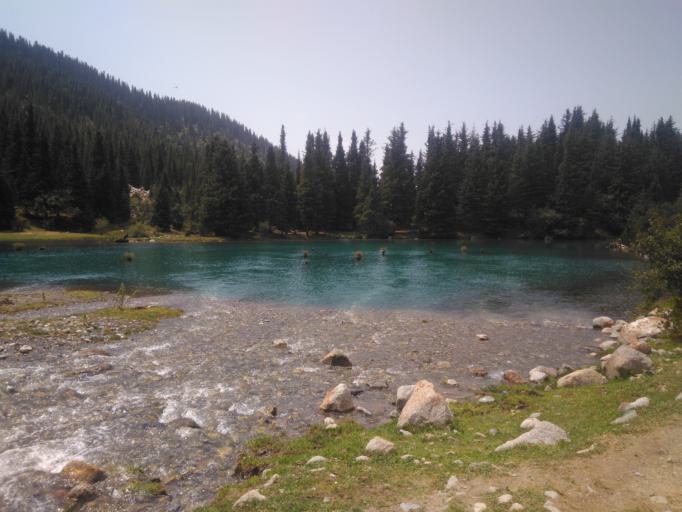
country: KG
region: Ysyk-Koel
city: Cholpon-Ata
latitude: 42.8412
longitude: 77.5679
